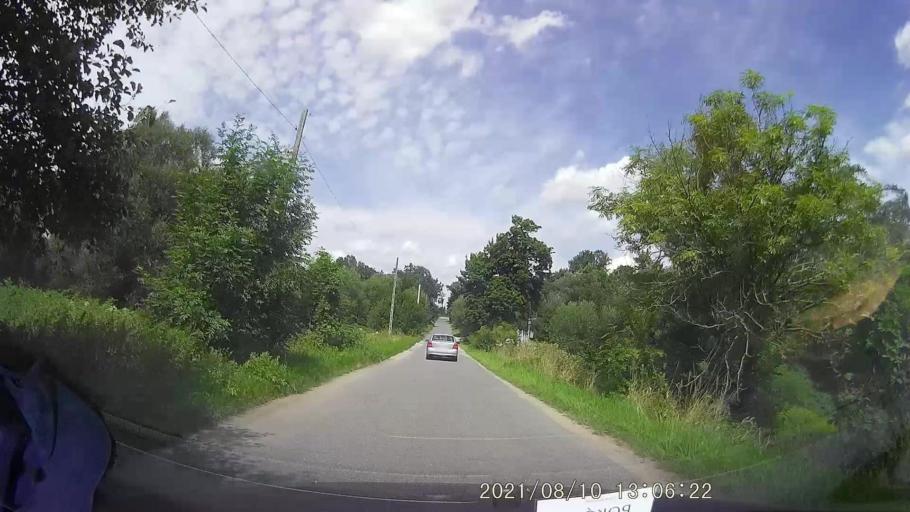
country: PL
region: Lower Silesian Voivodeship
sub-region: Powiat klodzki
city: Bozkow
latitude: 50.4859
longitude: 16.5726
